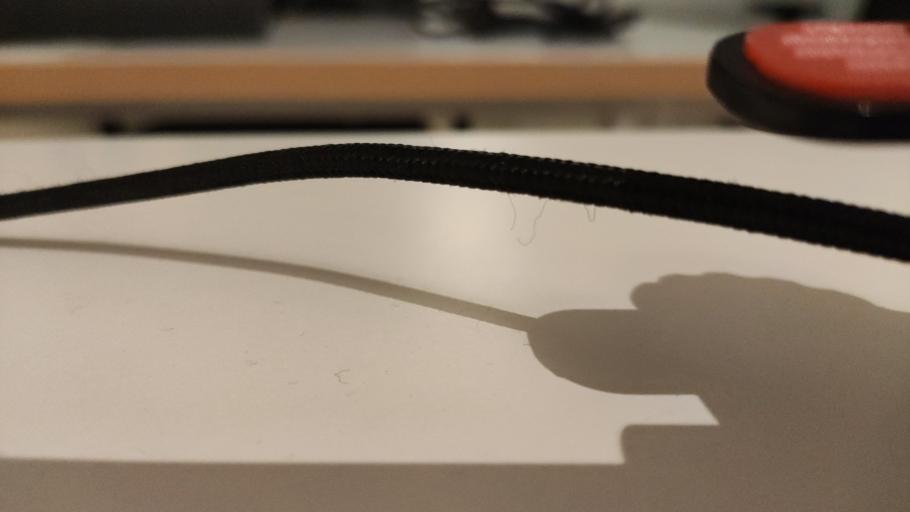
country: RU
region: Moskovskaya
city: Il'inskiy Pogost
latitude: 55.5195
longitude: 38.8718
